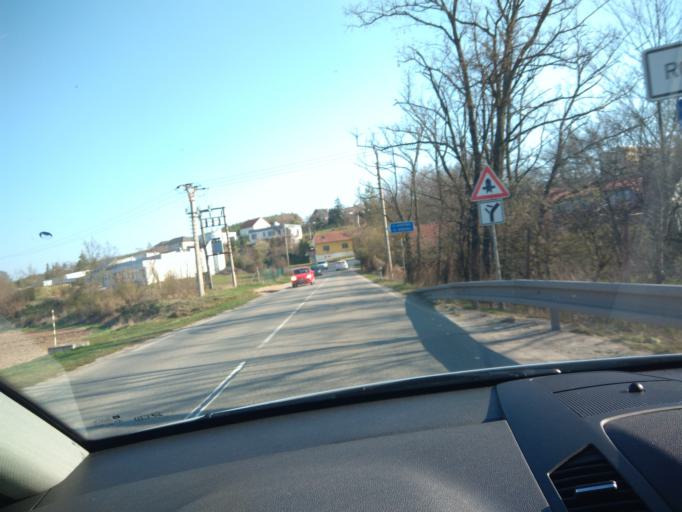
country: CZ
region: South Moravian
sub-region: Okres Brno-Venkov
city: Rosice
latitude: 49.1842
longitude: 16.3763
